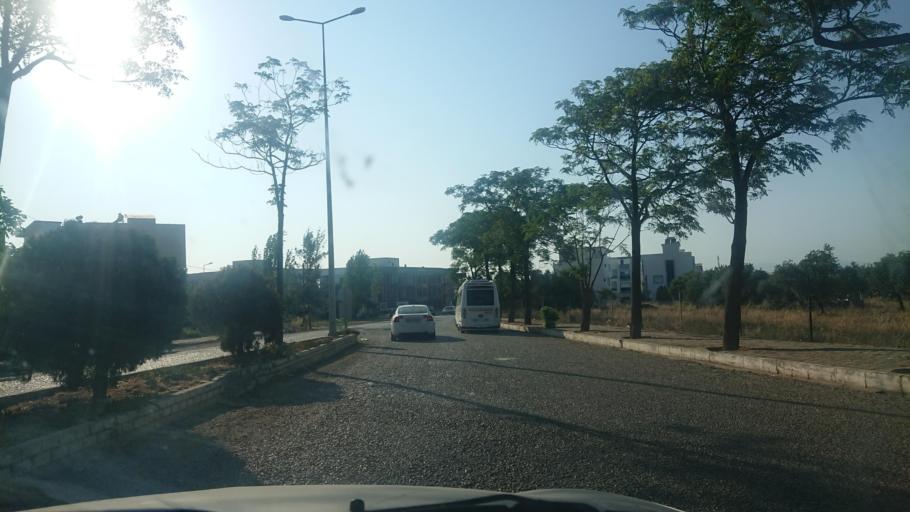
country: TR
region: Aydin
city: Davutlar
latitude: 37.7354
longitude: 27.2837
